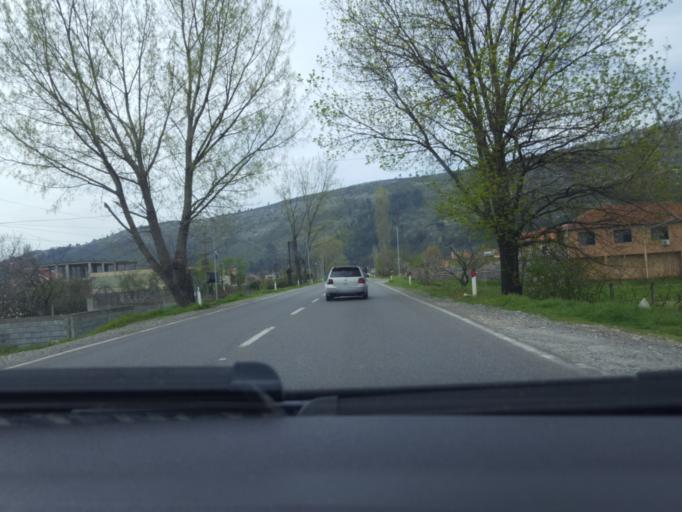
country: AL
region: Lezhe
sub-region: Rrethi i Lezhes
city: Balldreni i Ri
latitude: 41.8087
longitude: 19.6342
